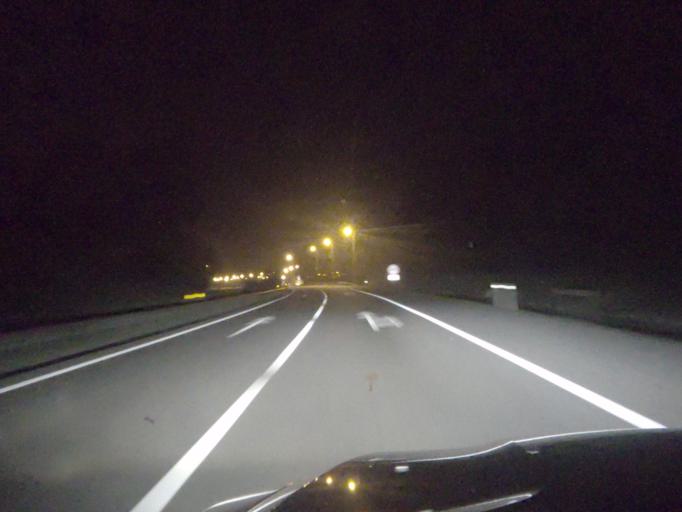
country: PT
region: Coimbra
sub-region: Soure
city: Soure
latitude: 40.0086
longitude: -8.6027
